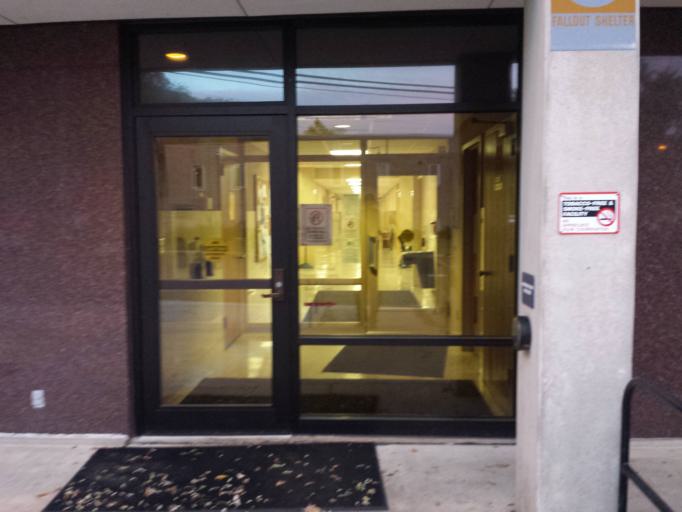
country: US
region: Wisconsin
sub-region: Buffalo County
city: Alma
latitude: 44.3199
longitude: -91.9133
